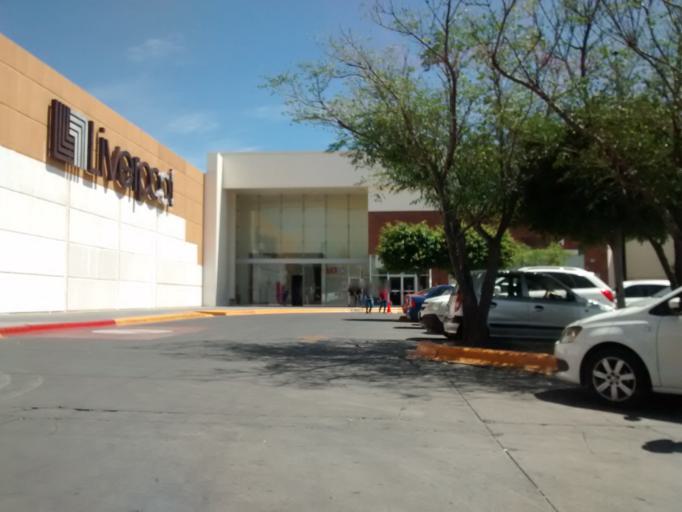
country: MX
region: Puebla
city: Tehuacan
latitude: 18.4682
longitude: -97.4167
